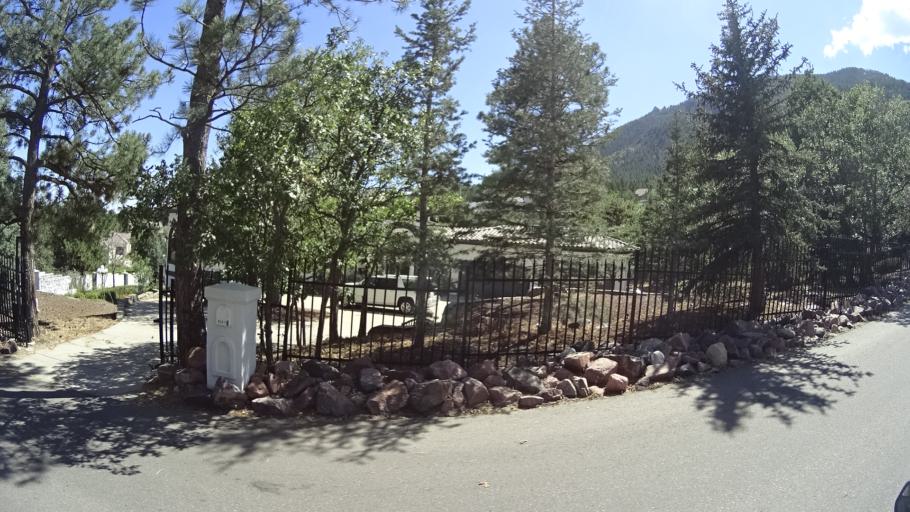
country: US
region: Colorado
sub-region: El Paso County
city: Colorado Springs
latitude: 38.7782
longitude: -104.8568
